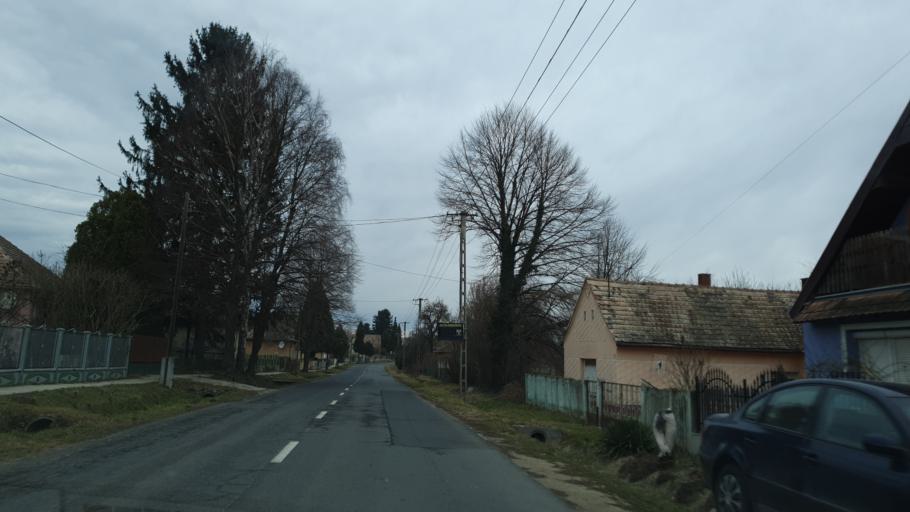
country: HU
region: Zala
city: Sarmellek
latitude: 46.6963
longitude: 17.1086
